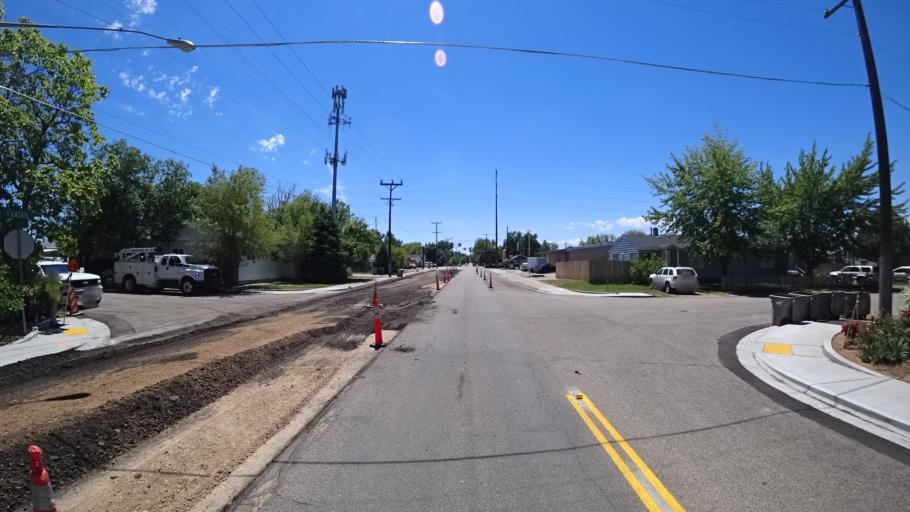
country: US
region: Idaho
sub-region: Ada County
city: Garden City
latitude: 43.5907
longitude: -116.2287
